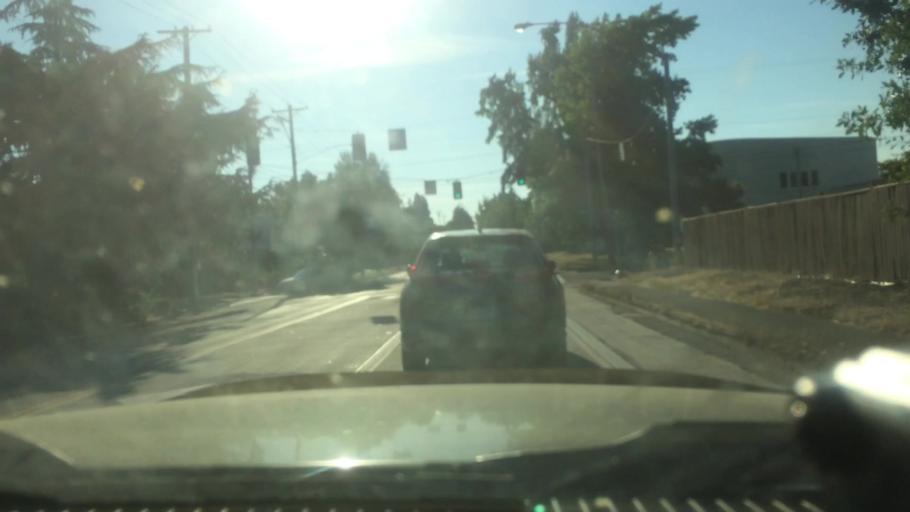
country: US
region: Oregon
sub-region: Lane County
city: Eugene
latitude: 44.0404
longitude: -123.1131
